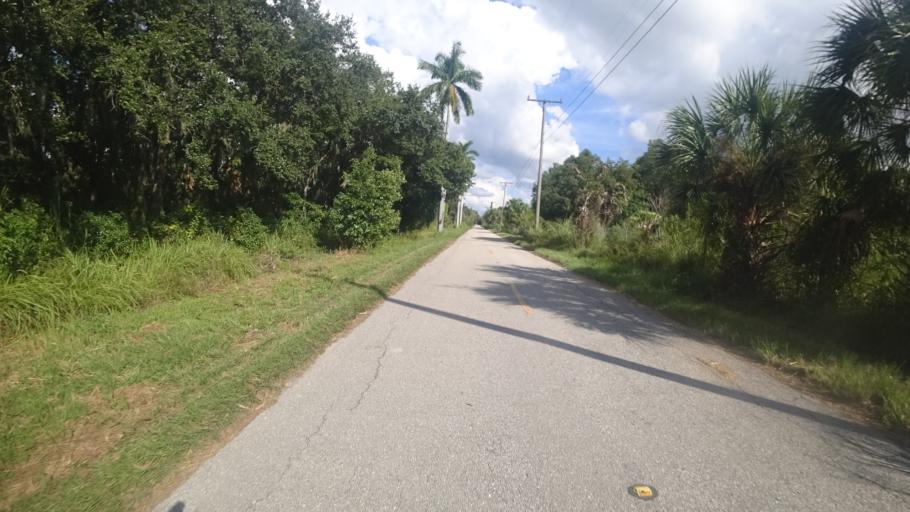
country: US
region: Florida
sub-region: Manatee County
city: Memphis
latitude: 27.5795
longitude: -82.5745
